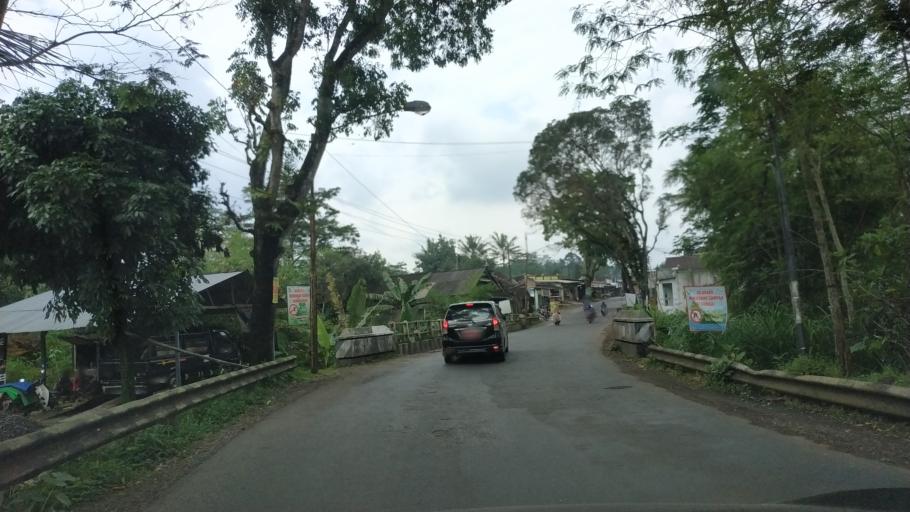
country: ID
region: Central Java
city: Weleri
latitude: -7.0937
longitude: 110.0549
